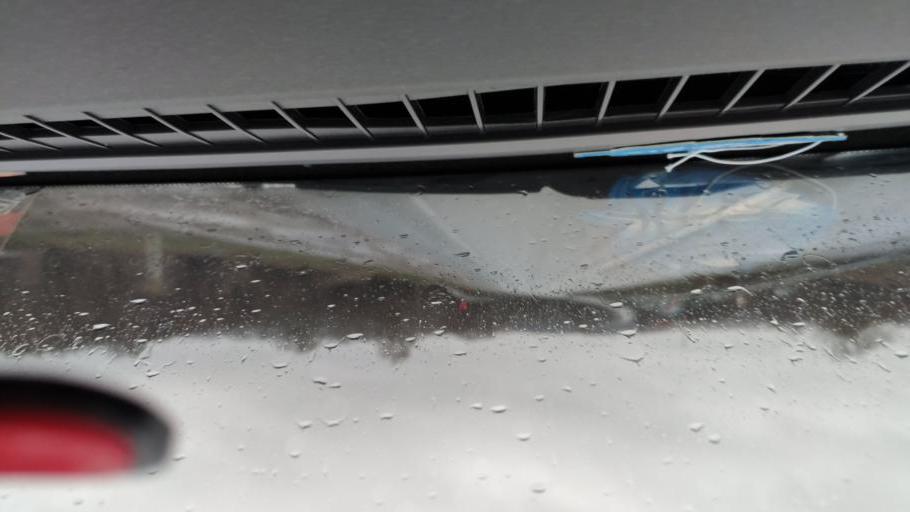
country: RU
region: Tatarstan
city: Mendeleyevsk
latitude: 55.8593
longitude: 52.2123
